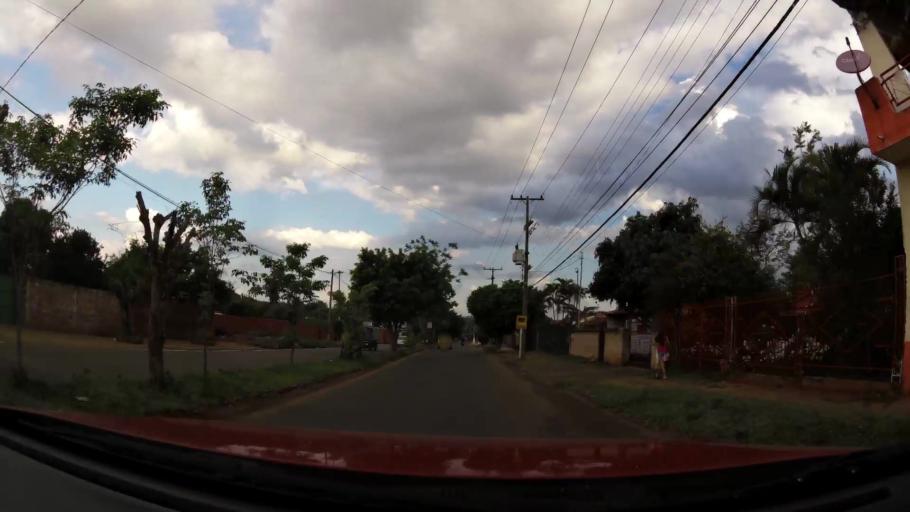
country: PY
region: Central
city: Nemby
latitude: -25.3693
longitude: -57.5550
